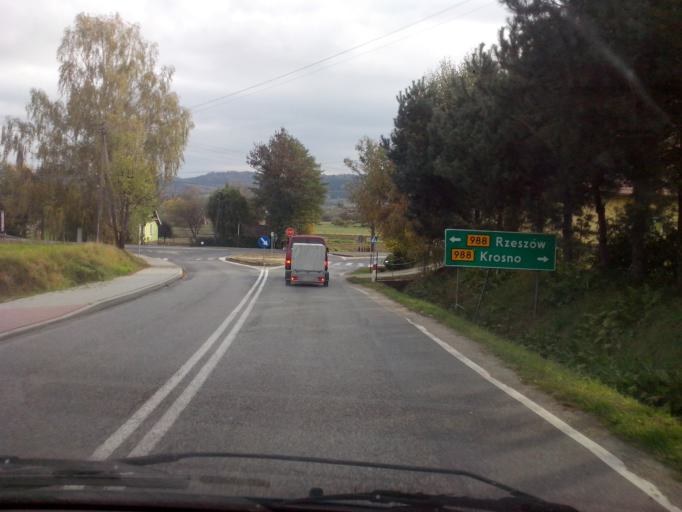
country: PL
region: Subcarpathian Voivodeship
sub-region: Powiat strzyzowski
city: Wisniowa
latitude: 49.8696
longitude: 21.6599
